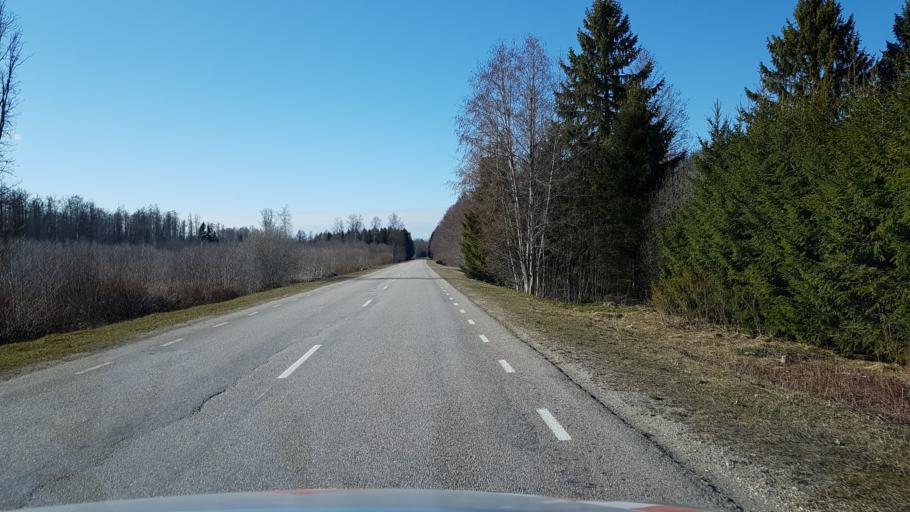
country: EE
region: Laeaene-Virumaa
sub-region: Haljala vald
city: Haljala
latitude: 59.5151
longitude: 26.0965
